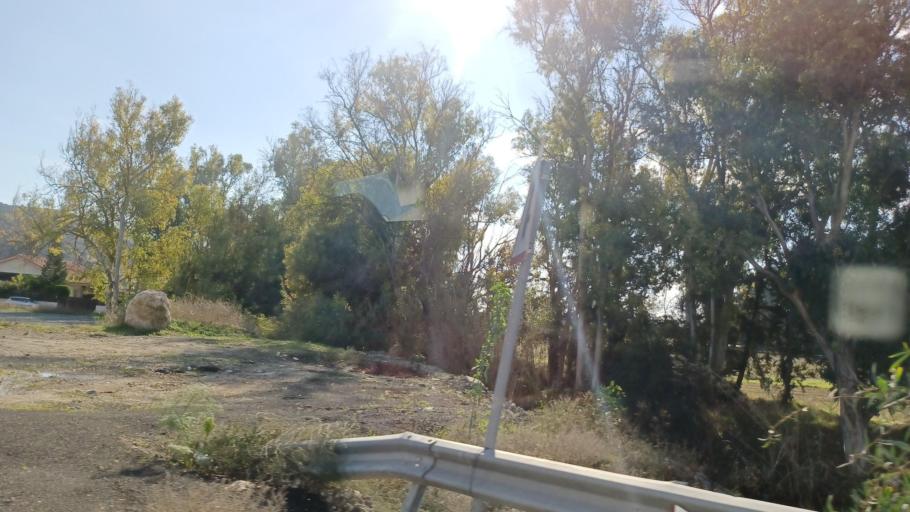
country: CY
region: Limassol
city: Pyrgos
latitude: 34.7211
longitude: 33.1987
